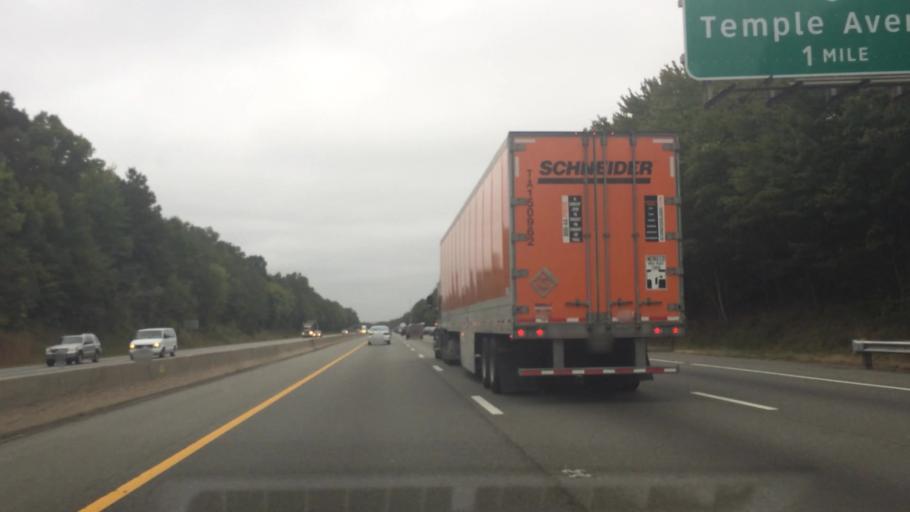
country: US
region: Virginia
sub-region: City of Colonial Heights
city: Colonial Heights
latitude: 37.2720
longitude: -77.3932
